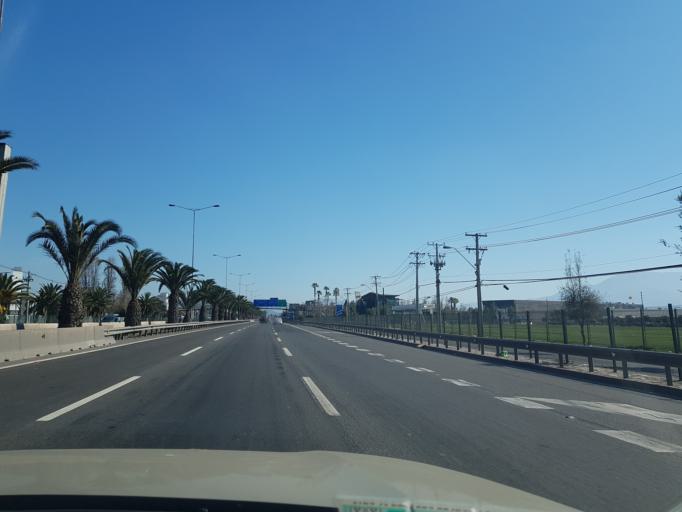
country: CL
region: Santiago Metropolitan
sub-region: Provincia de Santiago
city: Lo Prado
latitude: -33.3890
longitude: -70.7633
